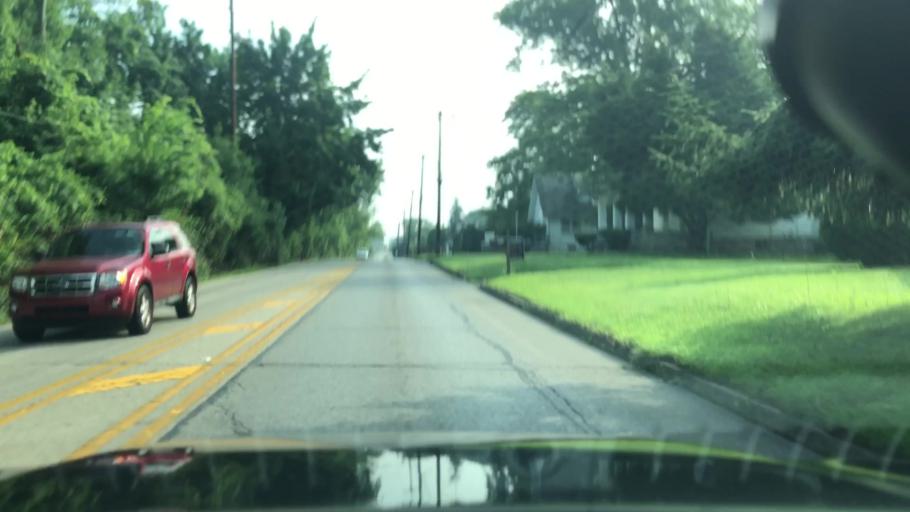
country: US
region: Pennsylvania
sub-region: Montgomery County
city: Norristown
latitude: 40.1447
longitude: -75.3103
